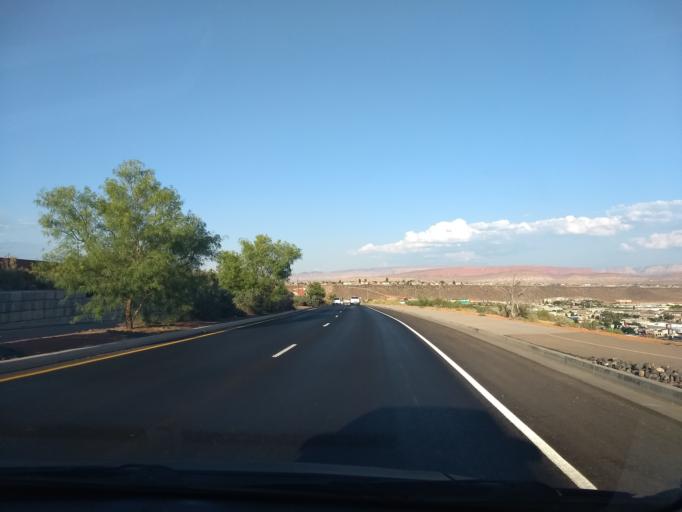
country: US
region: Utah
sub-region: Washington County
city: Saint George
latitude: 37.1125
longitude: -113.5701
